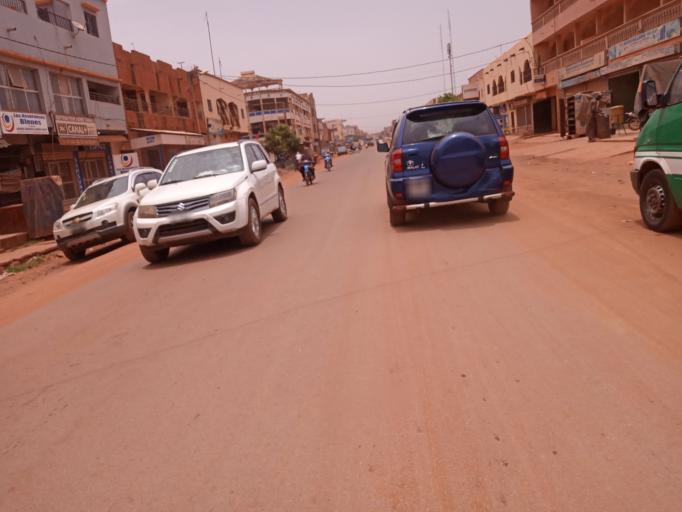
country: ML
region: Bamako
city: Bamako
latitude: 12.5831
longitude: -8.0226
